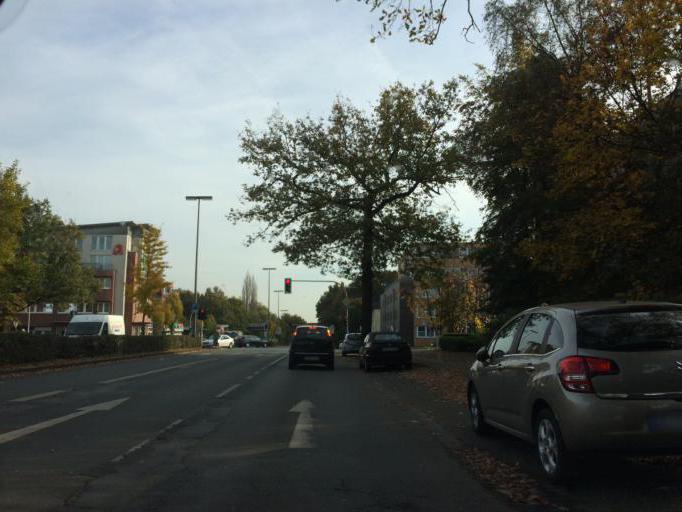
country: DE
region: North Rhine-Westphalia
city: Dorsten
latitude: 51.6695
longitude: 6.9705
